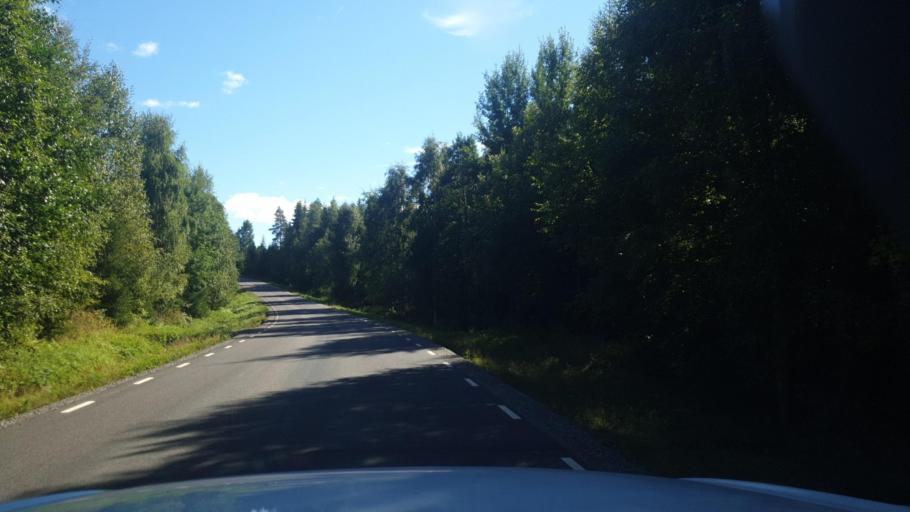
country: SE
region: Vaermland
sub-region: Torsby Kommun
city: Torsby
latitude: 59.9937
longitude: 12.7412
